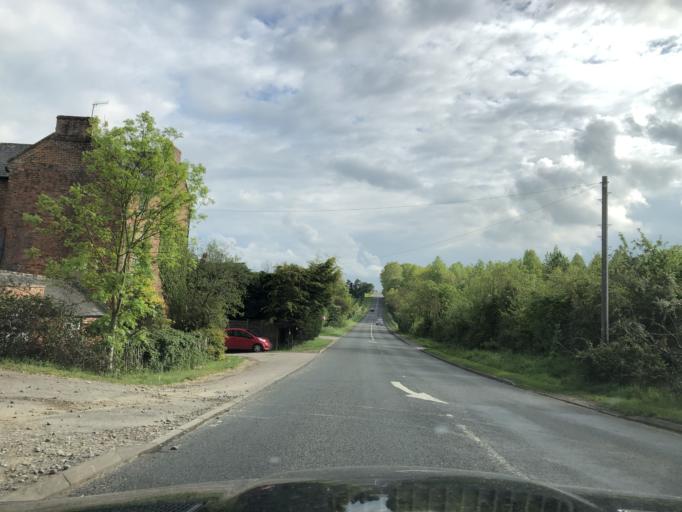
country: GB
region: England
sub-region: Warwickshire
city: Shipston on Stour
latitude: 52.0450
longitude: -1.6689
